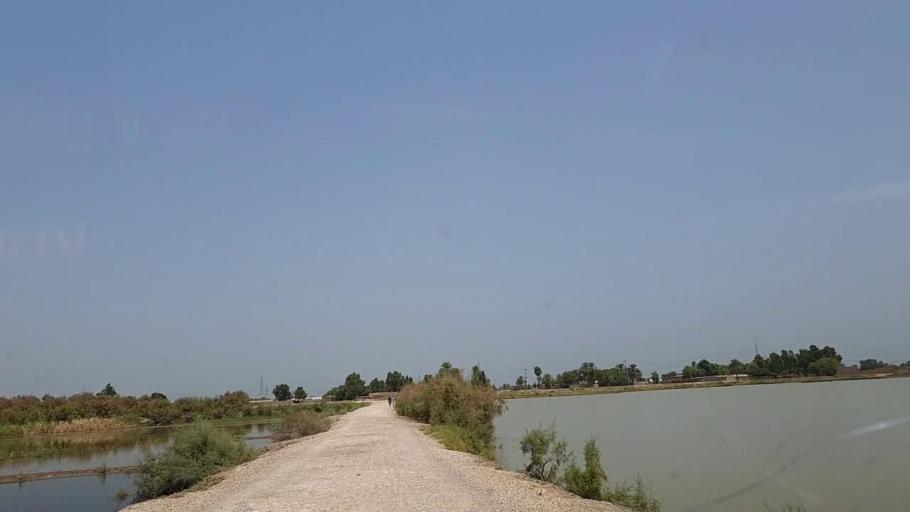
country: PK
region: Sindh
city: Ghotki
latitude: 27.9892
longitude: 69.3686
